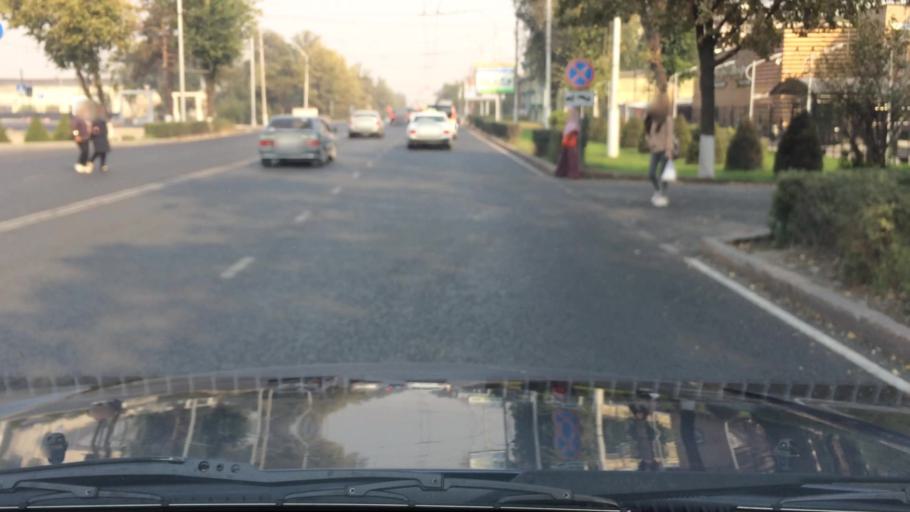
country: KG
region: Chuy
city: Bishkek
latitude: 42.8553
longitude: 74.5868
